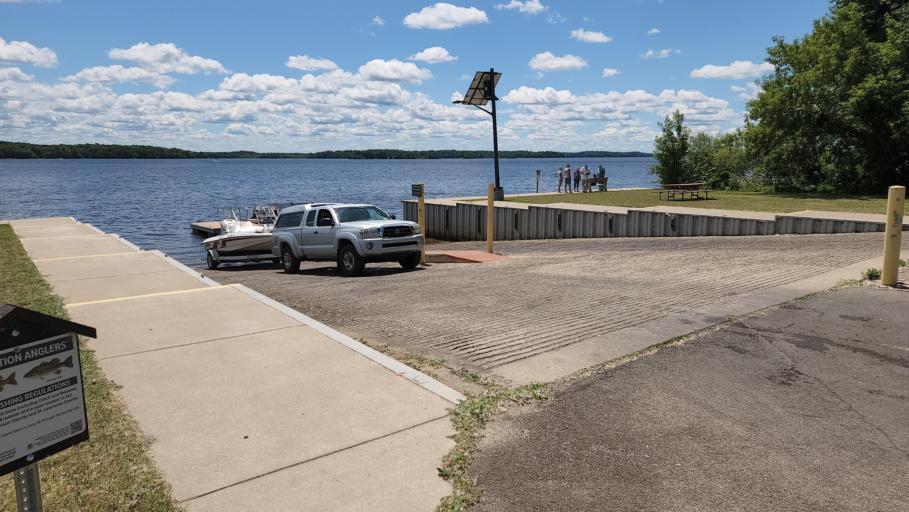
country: CA
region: Ontario
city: Brockville
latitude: 44.5100
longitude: -75.6117
